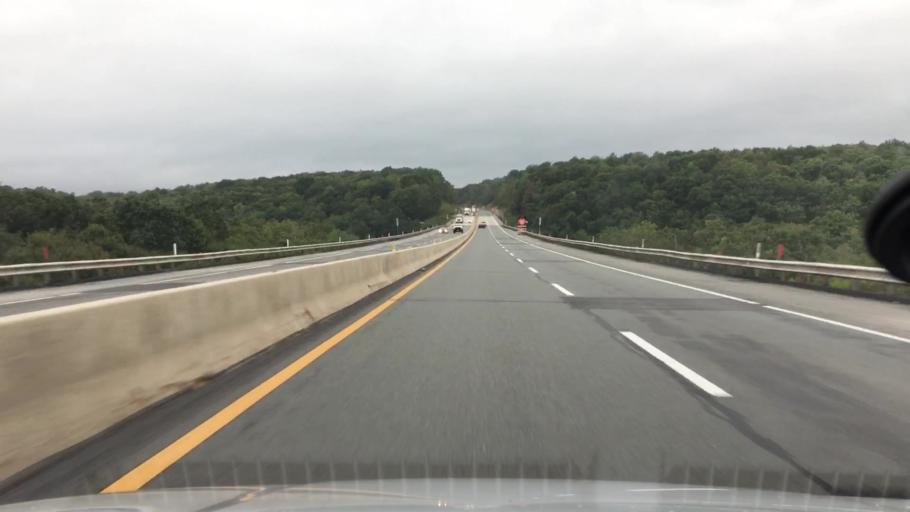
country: US
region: Pennsylvania
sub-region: Luzerne County
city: White Haven
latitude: 41.1014
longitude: -75.7472
